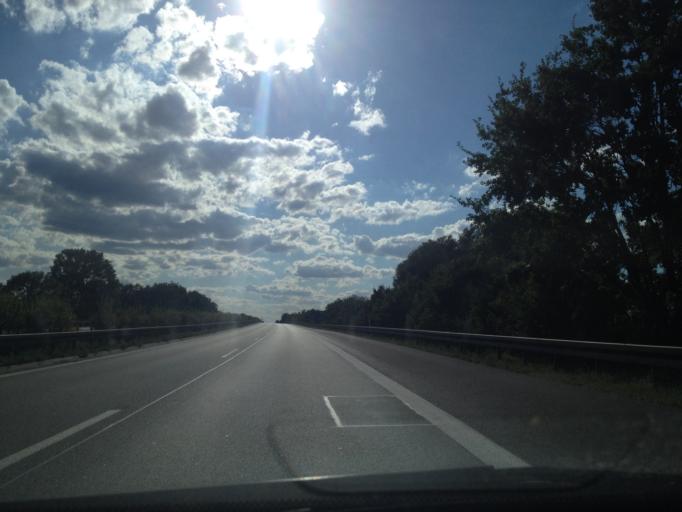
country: DE
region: Brandenburg
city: Kolkwitz
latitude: 51.7249
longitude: 14.2885
